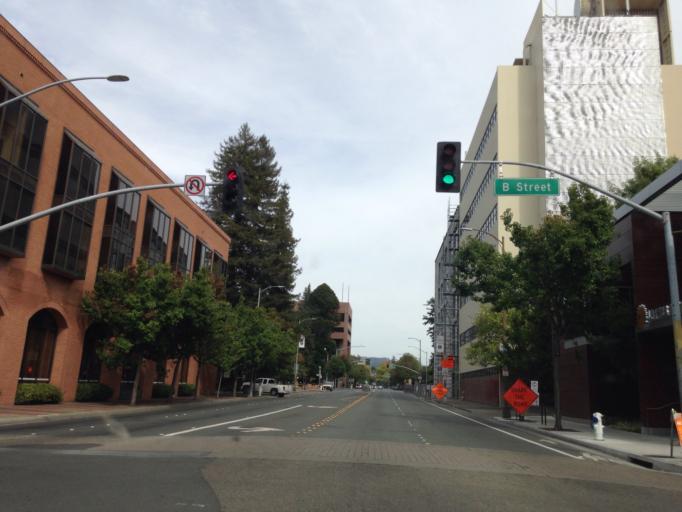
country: US
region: California
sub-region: Sonoma County
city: Santa Rosa
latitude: 38.4388
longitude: -122.7153
